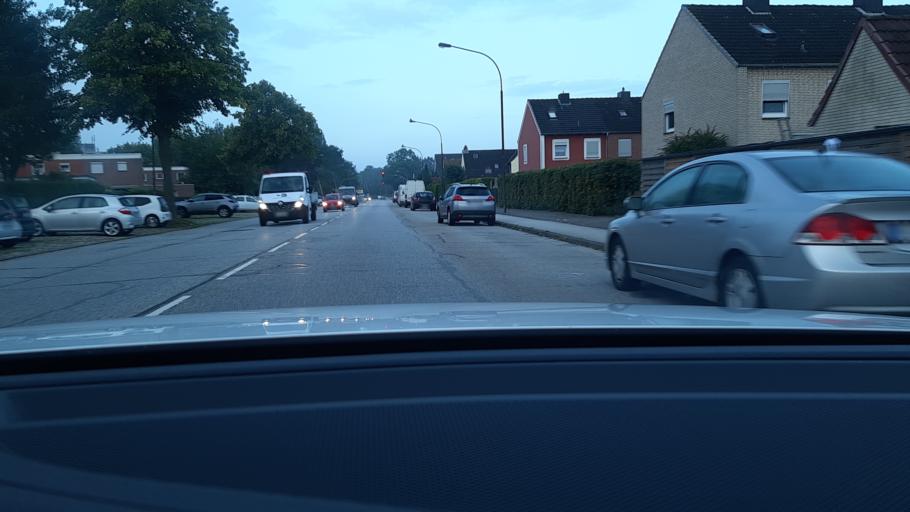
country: DE
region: Schleswig-Holstein
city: Stockelsdorf
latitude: 53.8583
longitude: 10.6440
